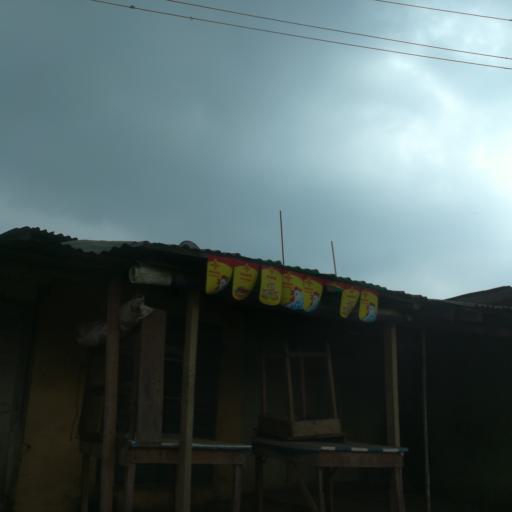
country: NG
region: Lagos
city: Agege
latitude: 6.5880
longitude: 3.3075
